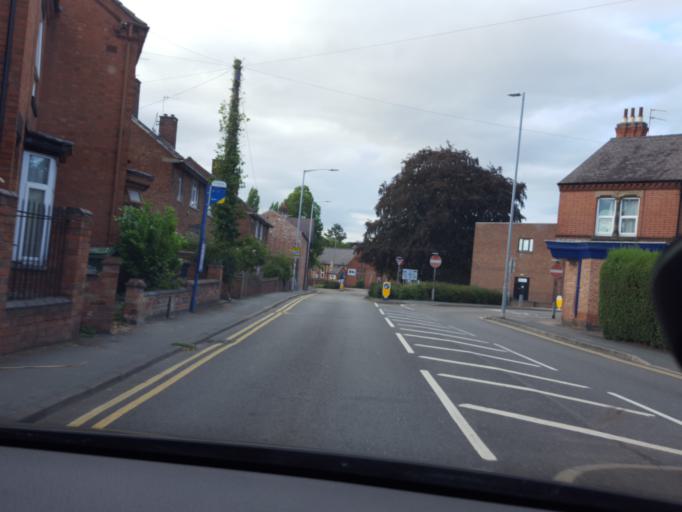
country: GB
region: England
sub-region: Leicestershire
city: Loughborough
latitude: 52.7663
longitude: -1.2089
